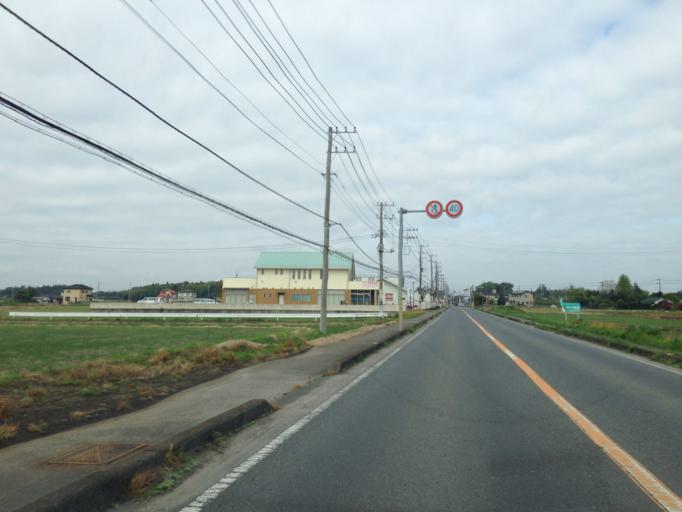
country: JP
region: Ibaraki
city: Tsukuba
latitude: 36.1365
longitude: 140.0624
